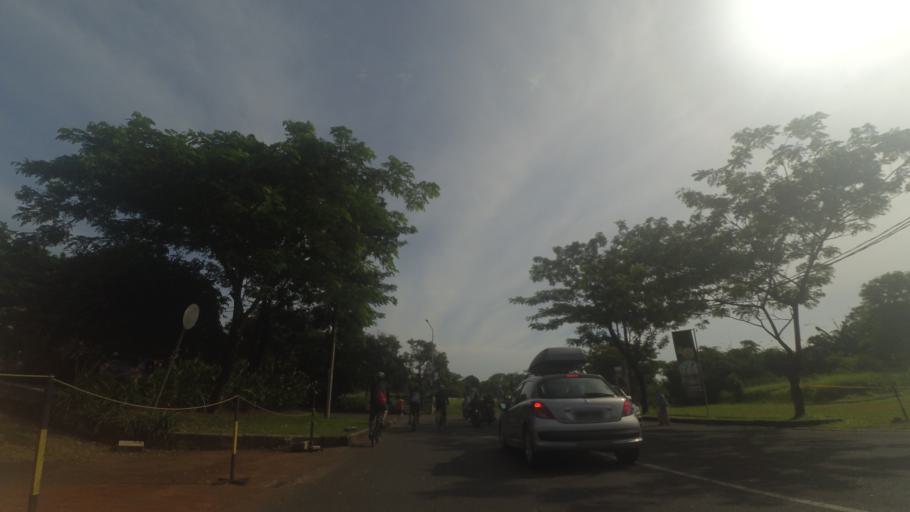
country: ID
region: West Java
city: Pamulang
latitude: -6.3436
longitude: 106.7682
